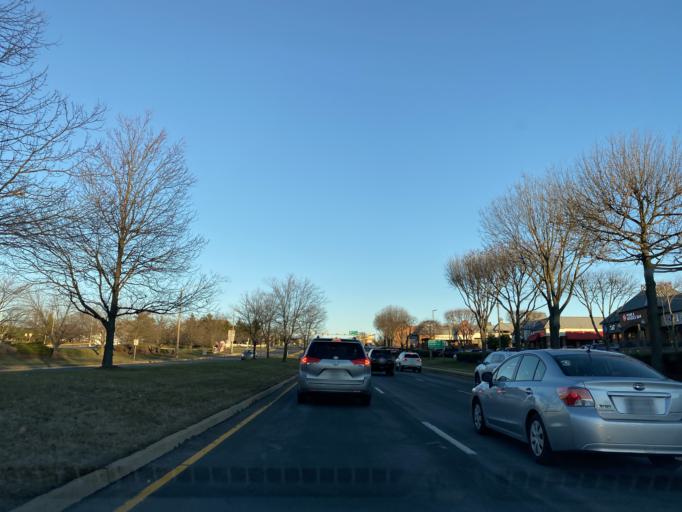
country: US
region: Virginia
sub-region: Fairfax County
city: Centreville
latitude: 38.8385
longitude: -77.4396
